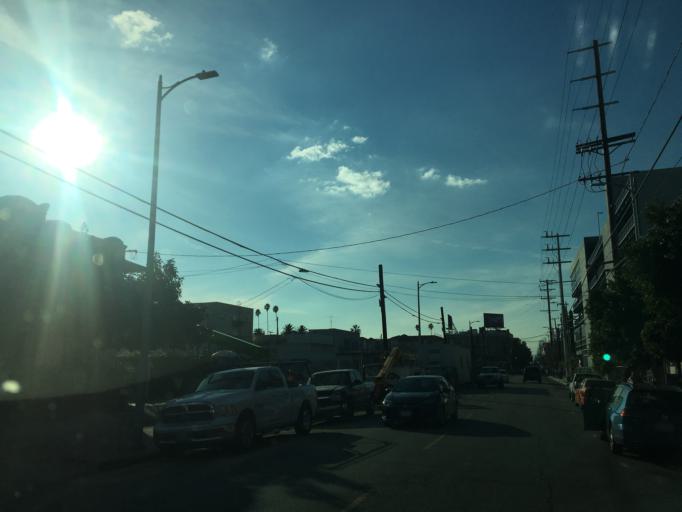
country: US
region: California
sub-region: Los Angeles County
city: Silver Lake
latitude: 34.0559
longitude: -118.2900
